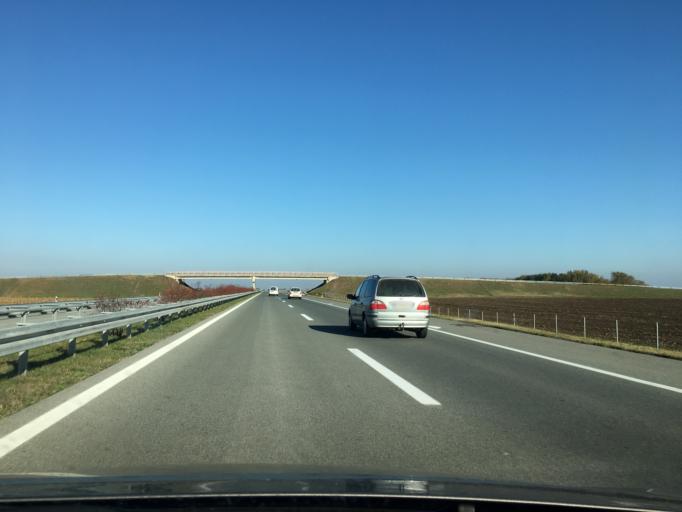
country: RS
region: Autonomna Pokrajina Vojvodina
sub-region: Severnobacki Okrug
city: Mali Igos
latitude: 45.7468
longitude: 19.7026
